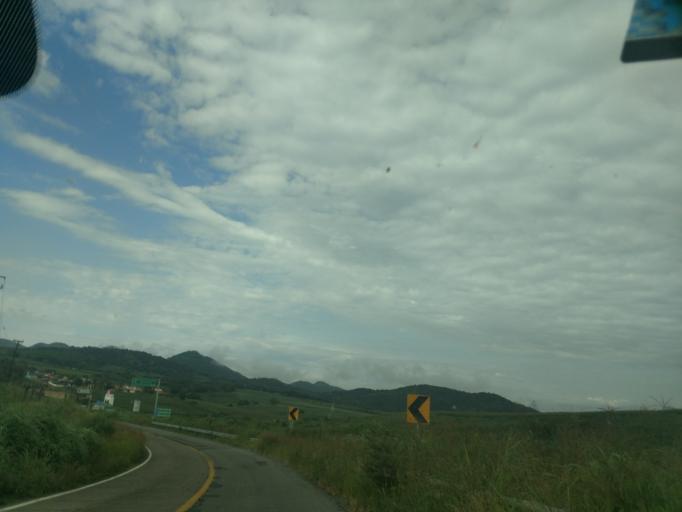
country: MX
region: Jalisco
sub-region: Atengo
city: Soyatlan del Oro
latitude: 20.5273
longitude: -104.3345
